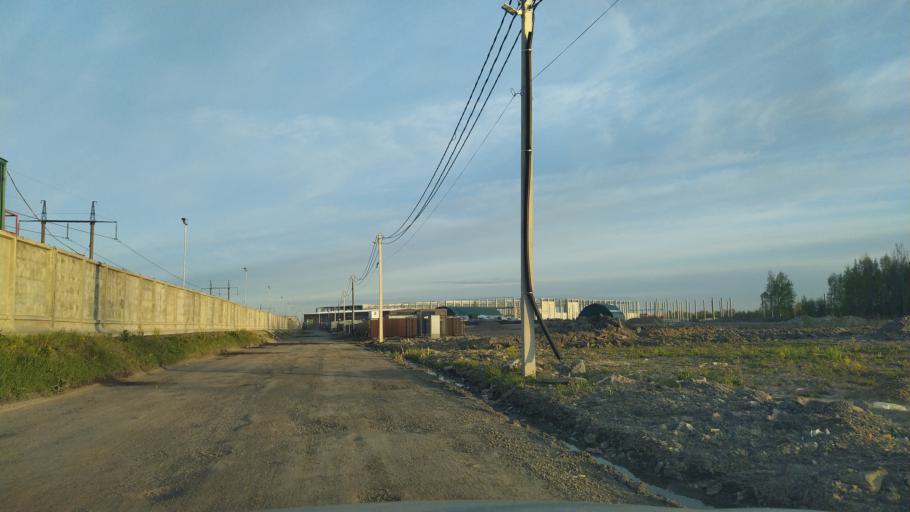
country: RU
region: St.-Petersburg
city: Obukhovo
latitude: 59.8047
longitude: 30.4597
